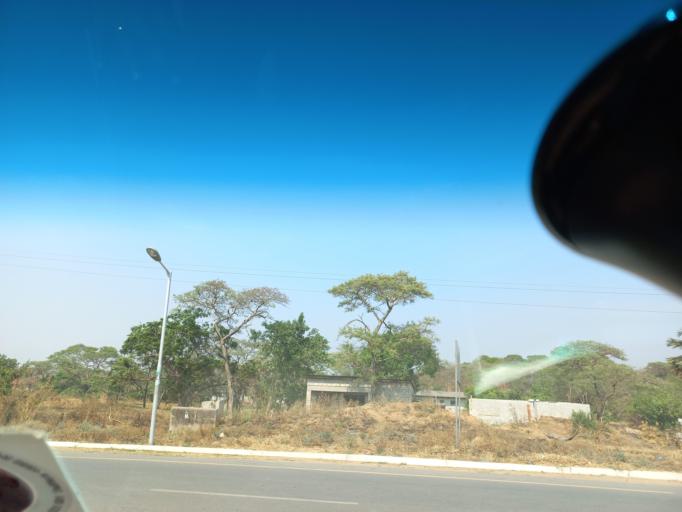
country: ZM
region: Lusaka
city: Lusaka
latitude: -15.5651
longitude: 28.2684
